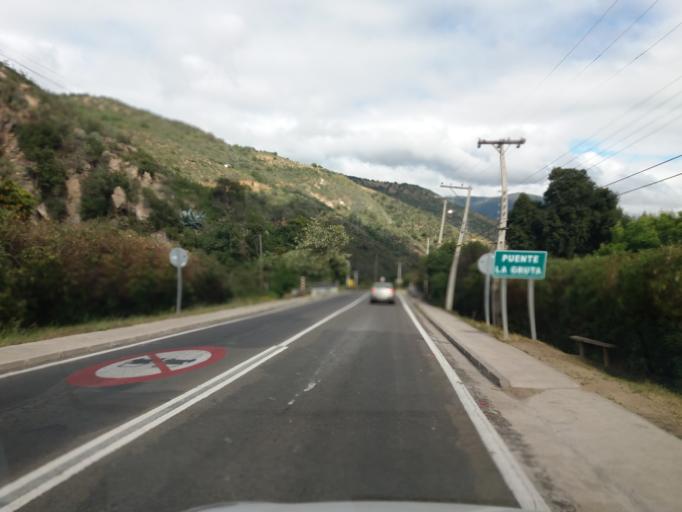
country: CL
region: Valparaiso
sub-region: Provincia de Marga Marga
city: Limache
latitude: -33.0630
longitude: -71.0679
